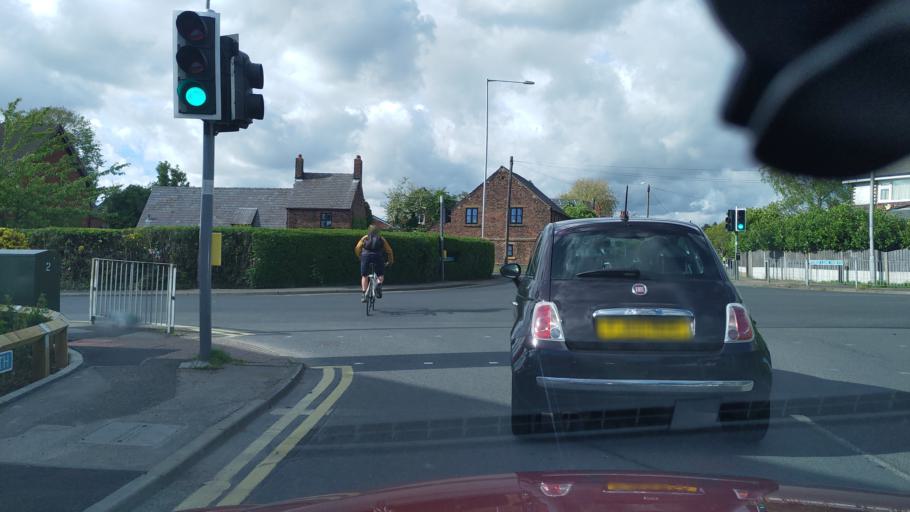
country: GB
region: England
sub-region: Lancashire
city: Leyland
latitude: 53.7273
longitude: -2.6819
